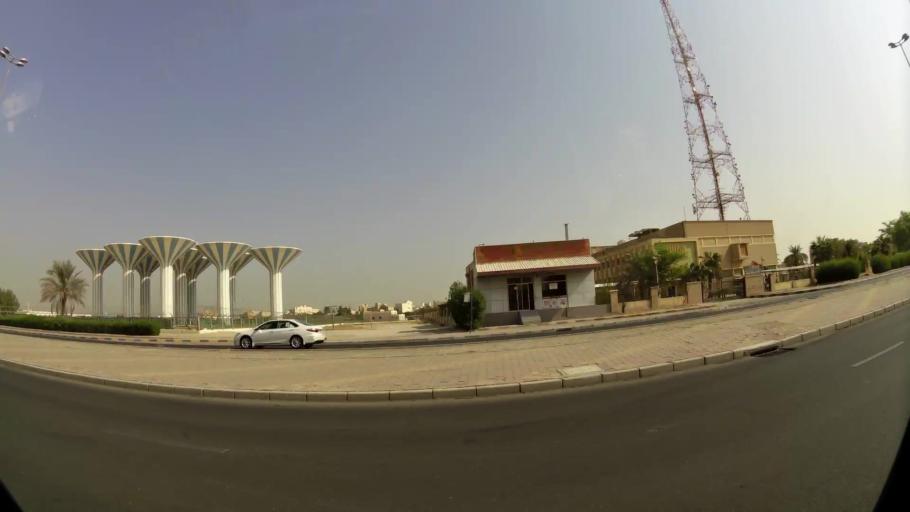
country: KW
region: Al Asimah
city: Ar Rabiyah
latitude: 29.2870
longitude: 47.8814
